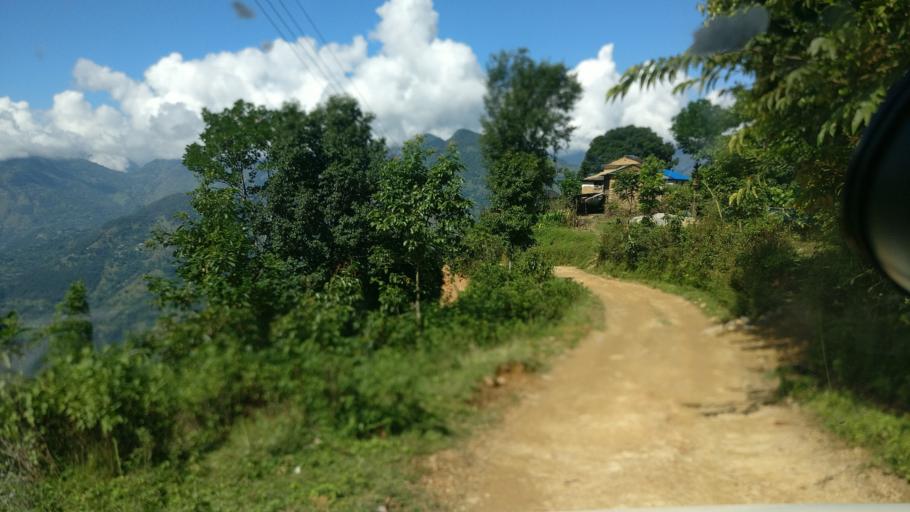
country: NP
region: Western Region
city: Baglung
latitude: 28.1336
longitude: 83.6584
